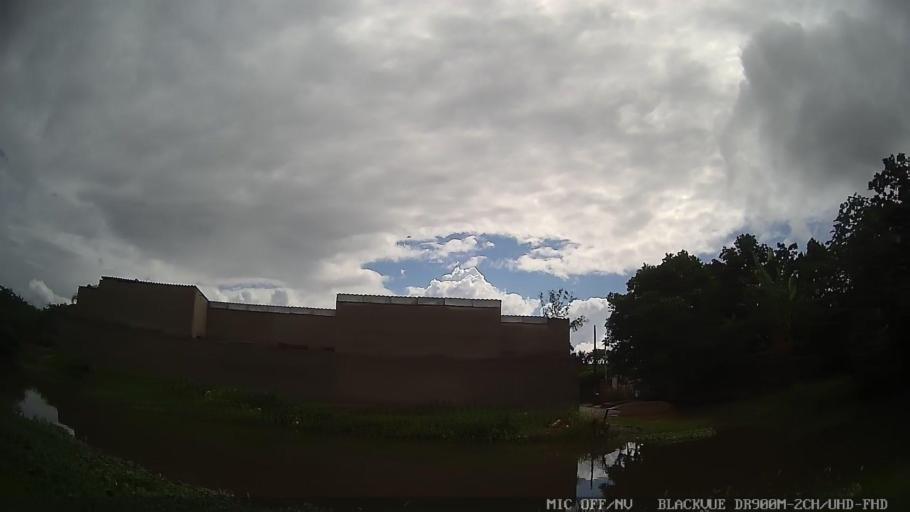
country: BR
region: Sao Paulo
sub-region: Itanhaem
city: Itanhaem
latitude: -24.1710
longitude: -46.7838
